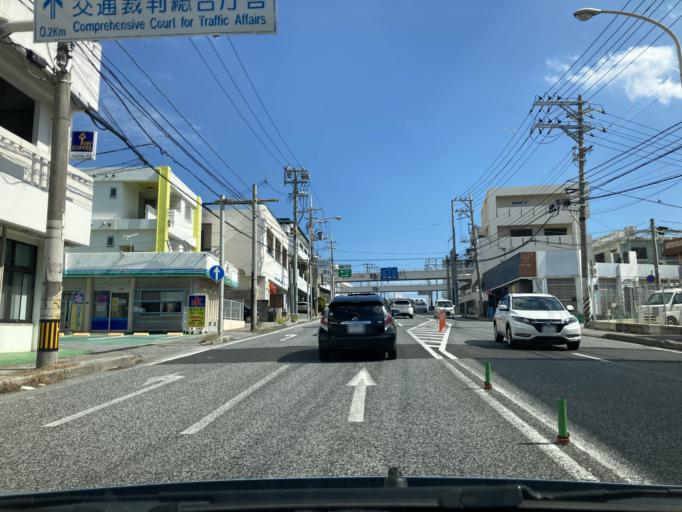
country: JP
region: Okinawa
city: Ginowan
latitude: 26.2566
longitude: 127.7525
